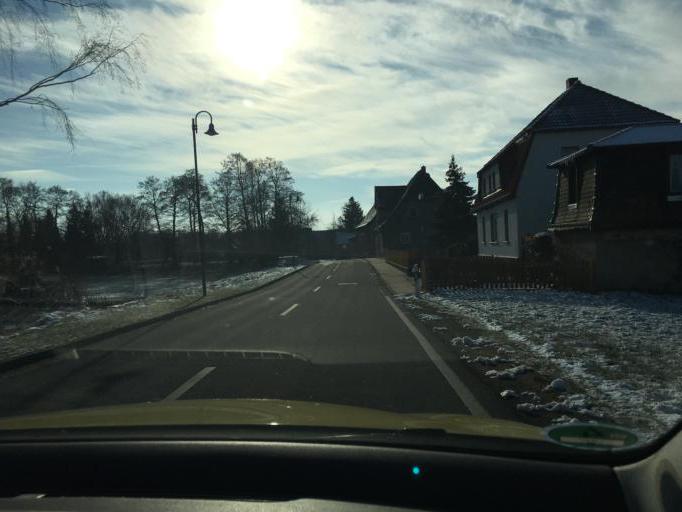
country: DE
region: Saxony
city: Belgershain
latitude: 51.2156
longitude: 12.5581
